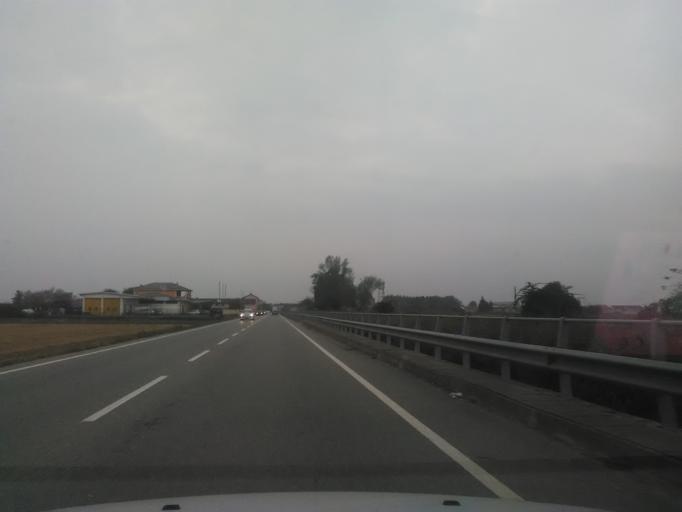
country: IT
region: Piedmont
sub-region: Provincia di Vercelli
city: San Germano Vercellese
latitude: 45.3473
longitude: 8.2591
